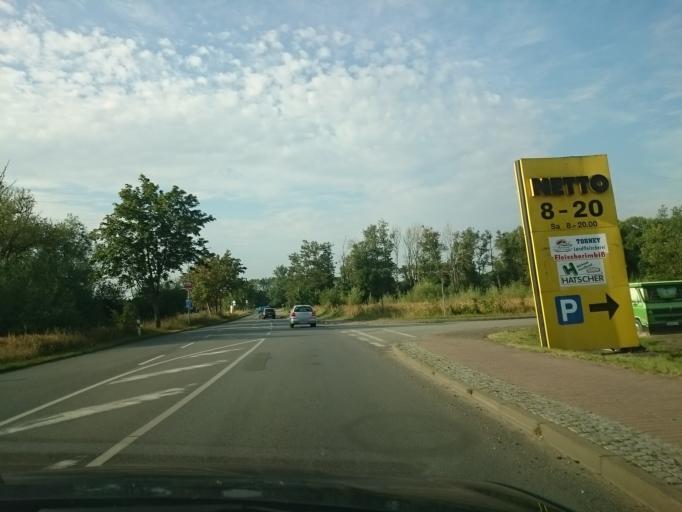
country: DE
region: Mecklenburg-Vorpommern
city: Demmin
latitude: 53.8988
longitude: 13.0416
